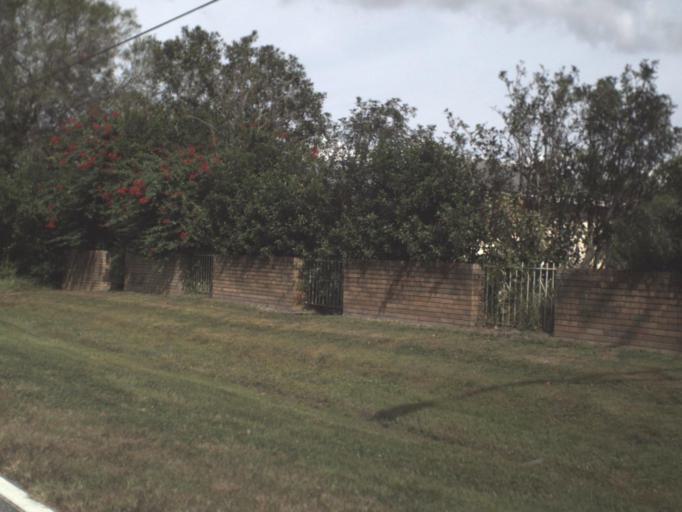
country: US
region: Florida
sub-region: Osceola County
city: Campbell
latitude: 28.2110
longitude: -81.4766
